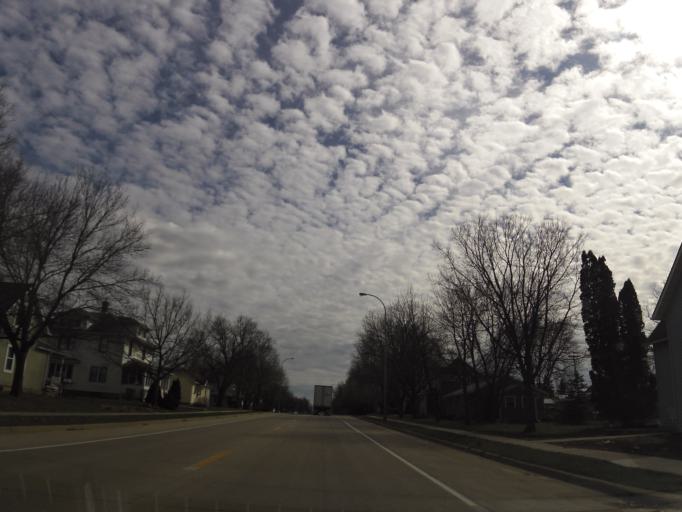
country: US
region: Minnesota
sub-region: Fillmore County
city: Spring Valley
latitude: 43.6833
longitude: -92.3893
